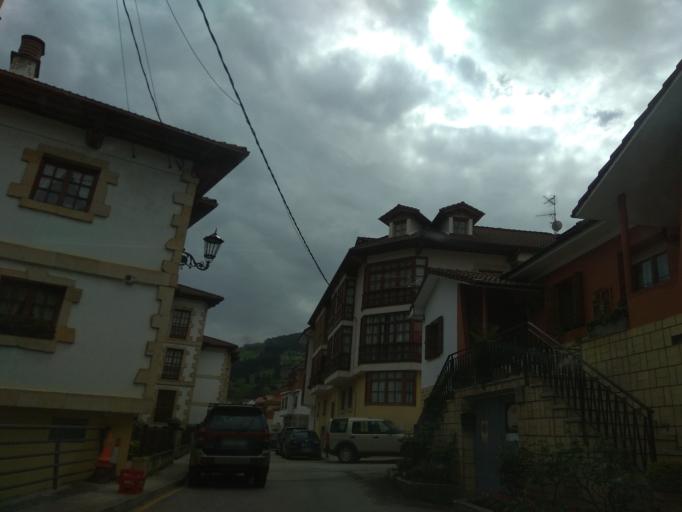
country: ES
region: Cantabria
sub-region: Provincia de Cantabria
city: Potes
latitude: 43.1539
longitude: -4.6279
